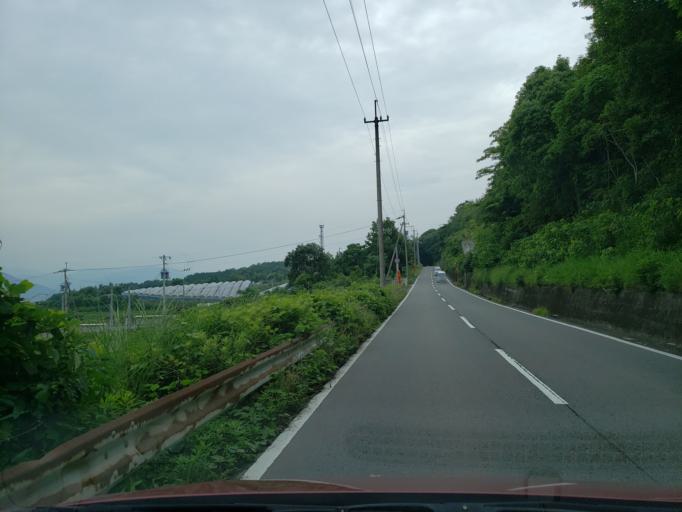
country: JP
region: Tokushima
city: Wakimachi
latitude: 34.1052
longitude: 134.2477
